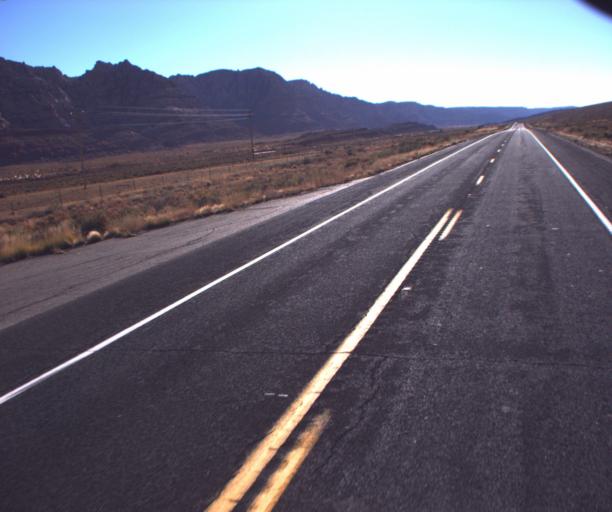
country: US
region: Arizona
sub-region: Coconino County
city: LeChee
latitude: 36.5536
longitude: -111.6289
